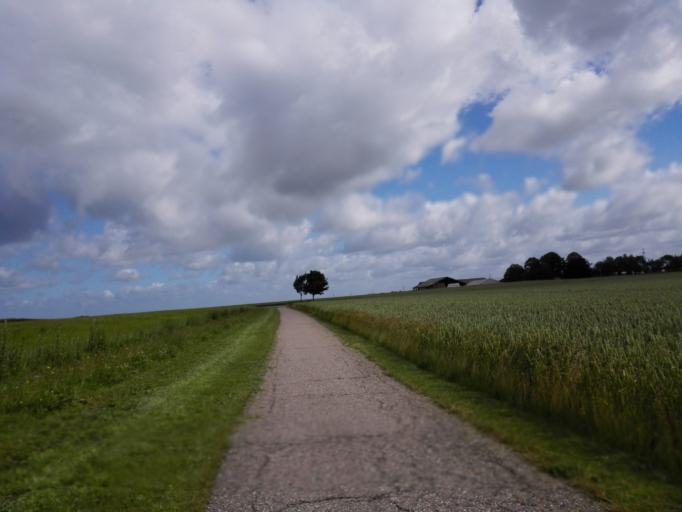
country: DK
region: Capital Region
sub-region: Egedal Kommune
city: Olstykke
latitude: 55.8056
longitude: 12.1505
